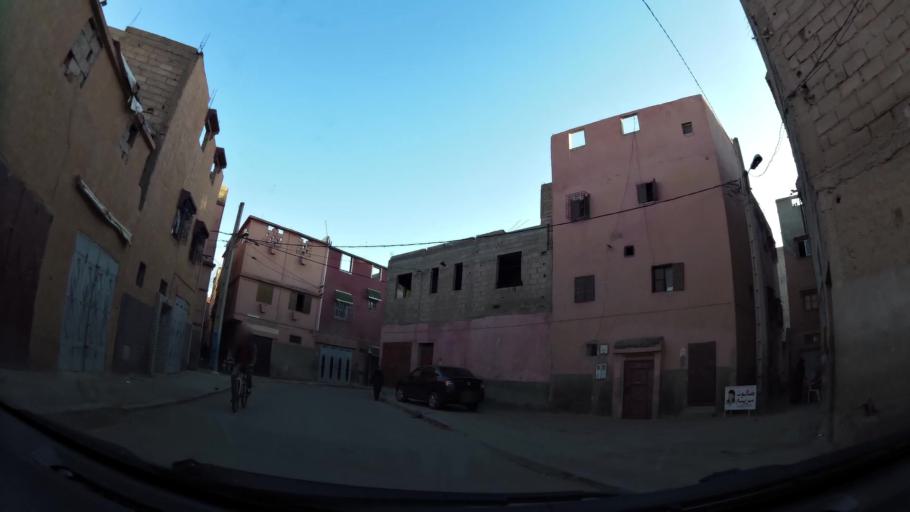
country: MA
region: Marrakech-Tensift-Al Haouz
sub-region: Kelaa-Des-Sraghna
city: Sidi Abdallah
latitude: 32.2445
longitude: -7.9522
